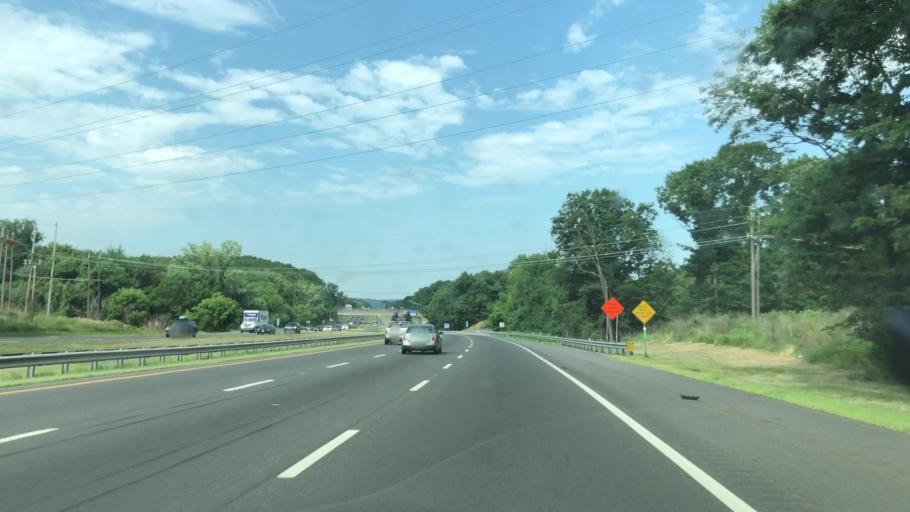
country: US
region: New Jersey
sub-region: Morris County
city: Wharton
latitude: 40.9088
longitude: -74.5966
